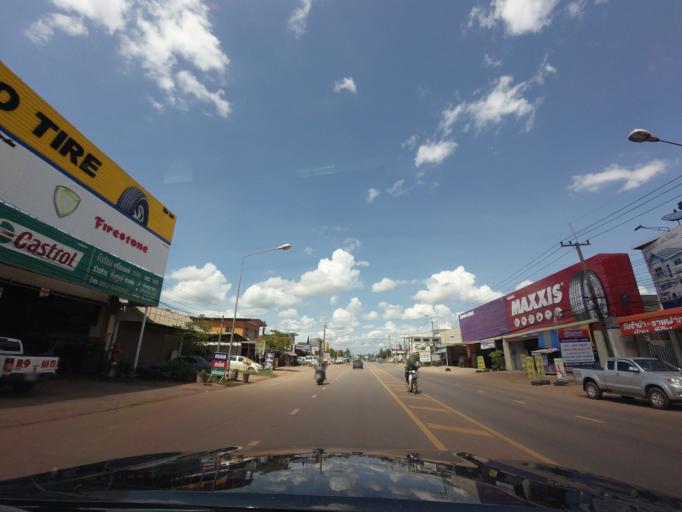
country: TH
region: Changwat Udon Thani
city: Ban Dung
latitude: 17.6858
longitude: 103.2561
